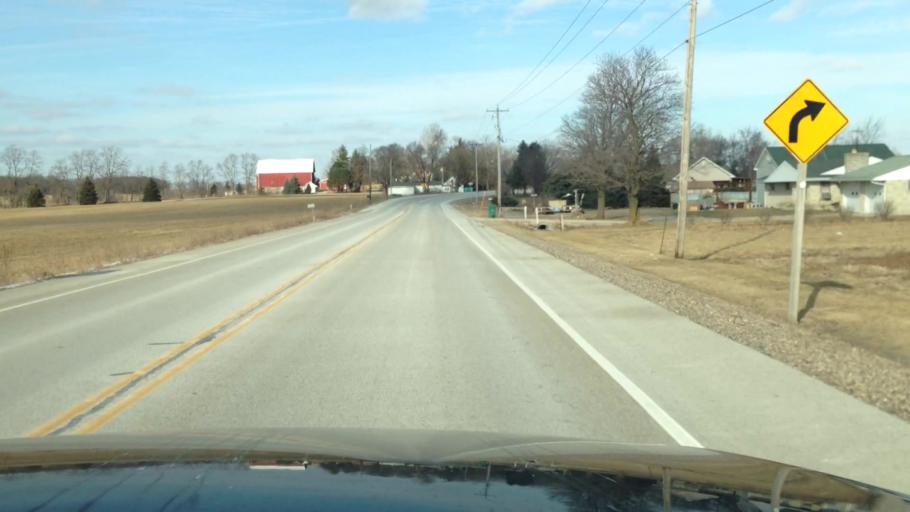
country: US
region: Wisconsin
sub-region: Walworth County
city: Lake Geneva
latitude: 42.6663
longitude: -88.4160
